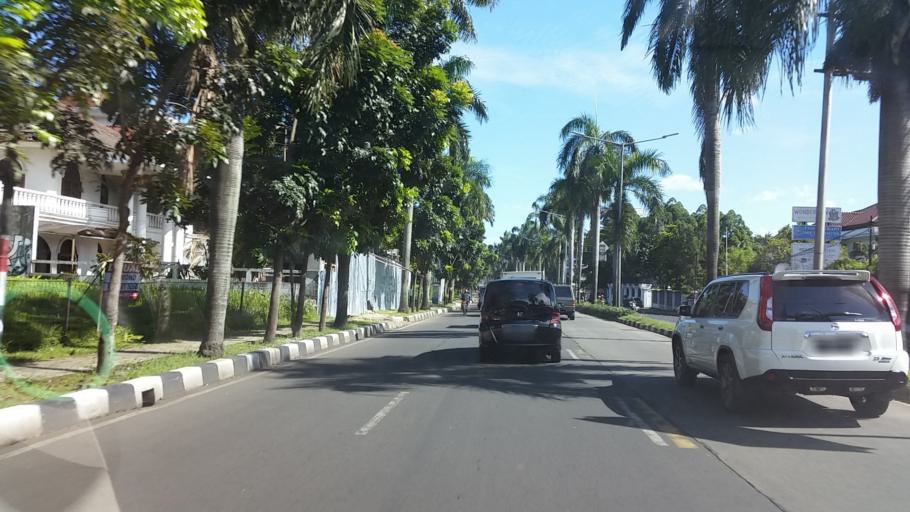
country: ID
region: Banten
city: South Tangerang
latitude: -6.2797
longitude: 106.7809
